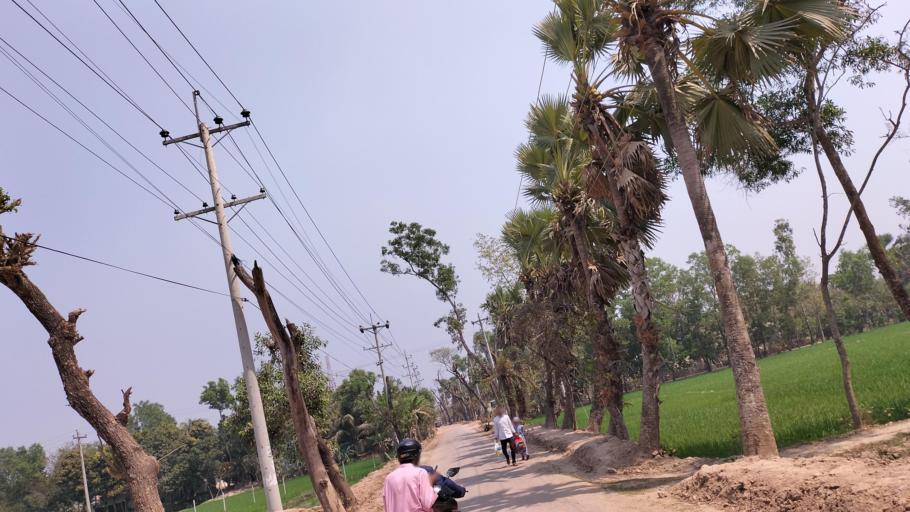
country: BD
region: Dhaka
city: Sakhipur
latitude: 24.3068
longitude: 90.3131
